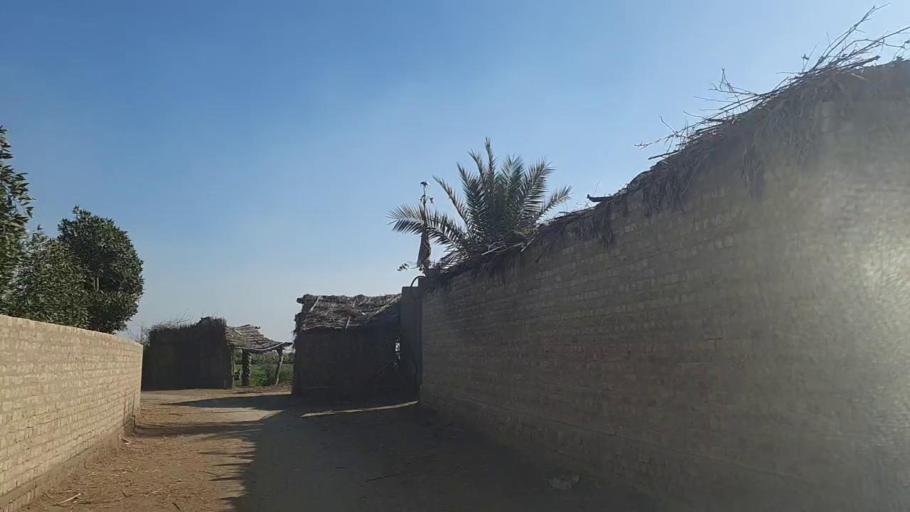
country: PK
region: Sindh
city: Jam Sahib
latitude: 26.2236
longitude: 68.6044
